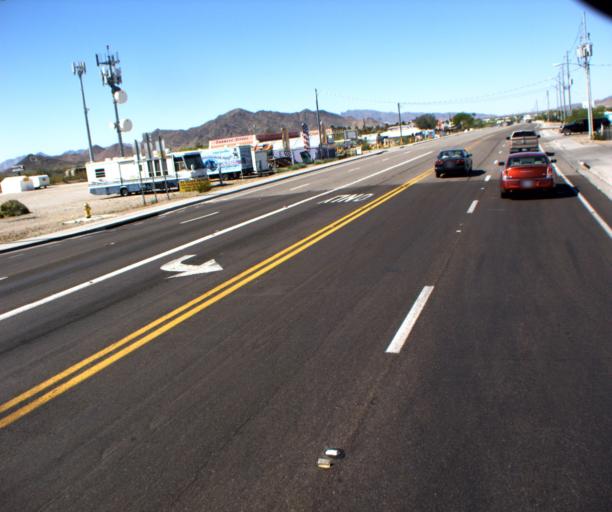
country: US
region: Arizona
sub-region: La Paz County
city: Quartzsite
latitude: 33.6667
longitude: -114.2173
